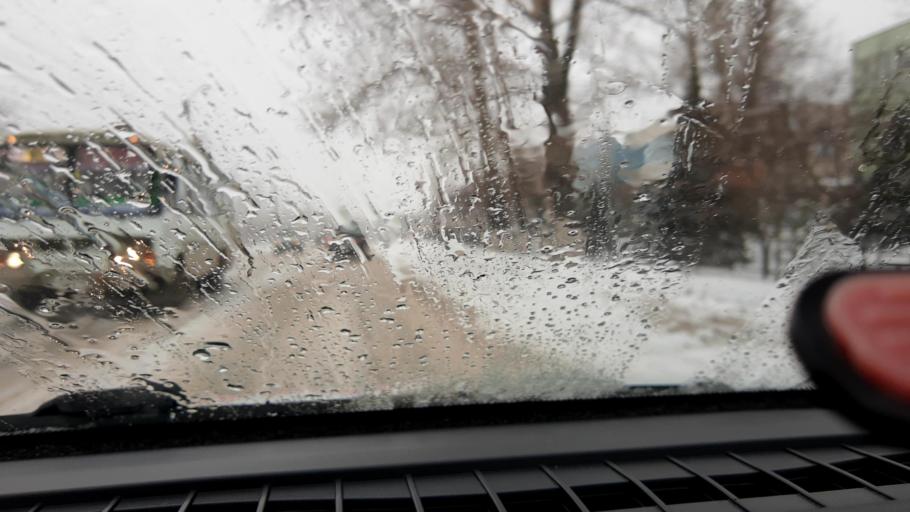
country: RU
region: Nizjnij Novgorod
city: Bor
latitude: 56.3490
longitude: 44.0801
